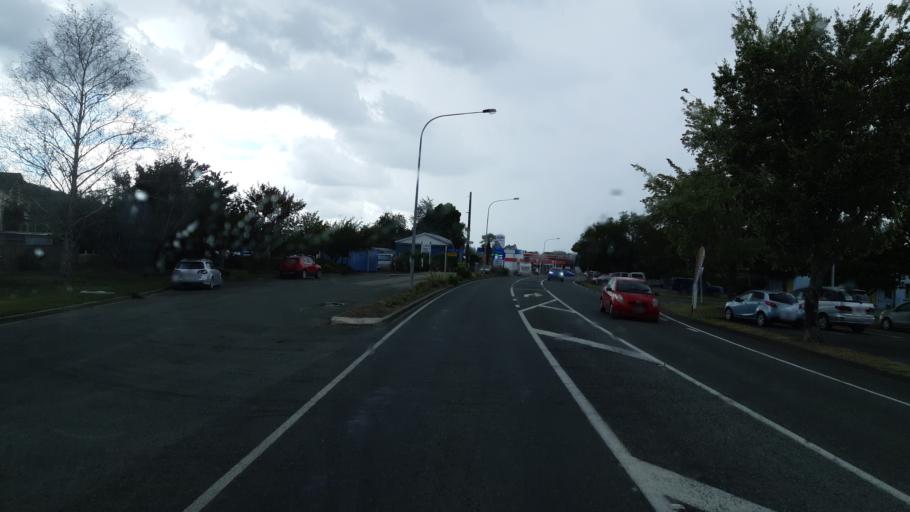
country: NZ
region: Tasman
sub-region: Tasman District
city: Wakefield
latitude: -41.4052
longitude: 173.0428
